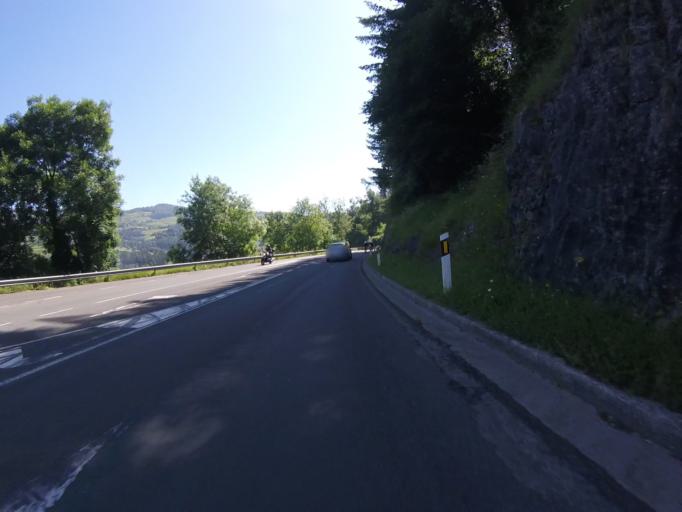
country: ES
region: Basque Country
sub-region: Provincia de Guipuzcoa
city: Albiztur
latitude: 43.1250
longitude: -2.1379
